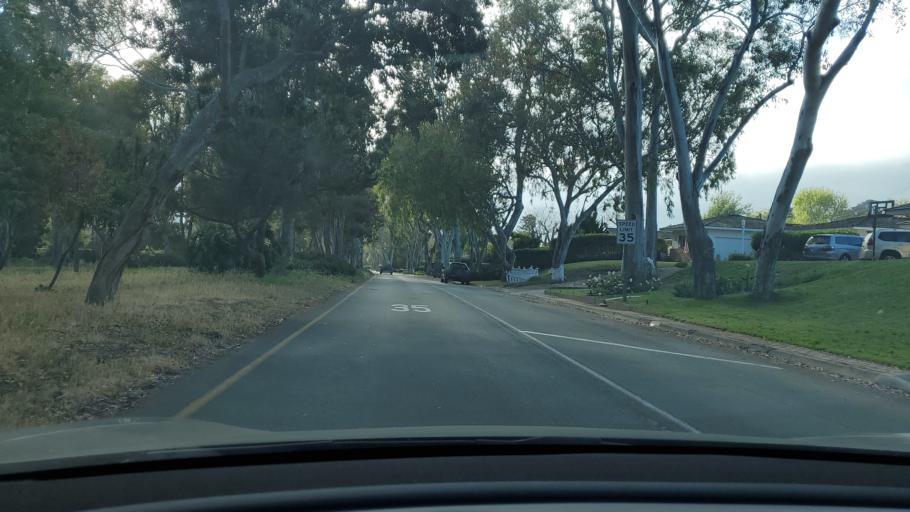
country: US
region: California
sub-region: Los Angeles County
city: Rolling Hills Estates
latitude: 33.8023
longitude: -118.3705
